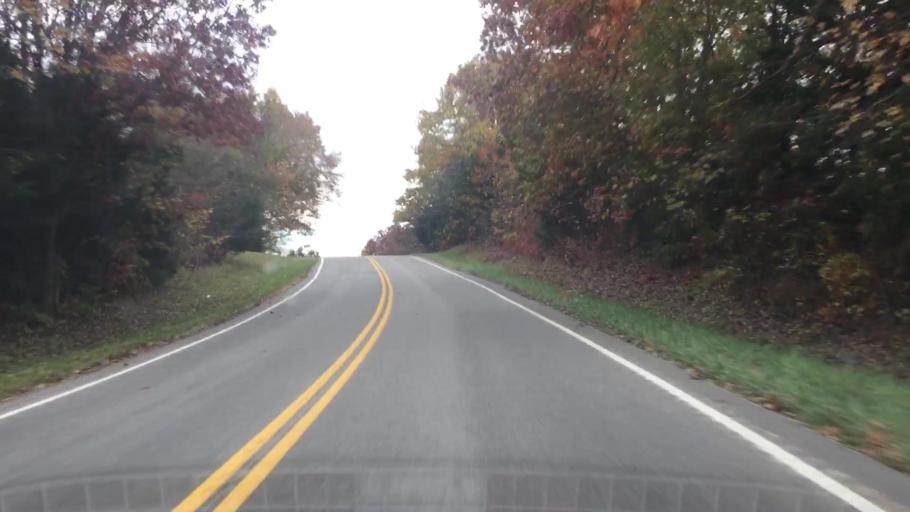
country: US
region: Missouri
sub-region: Gasconade County
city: Hermann
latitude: 38.7188
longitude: -91.7081
